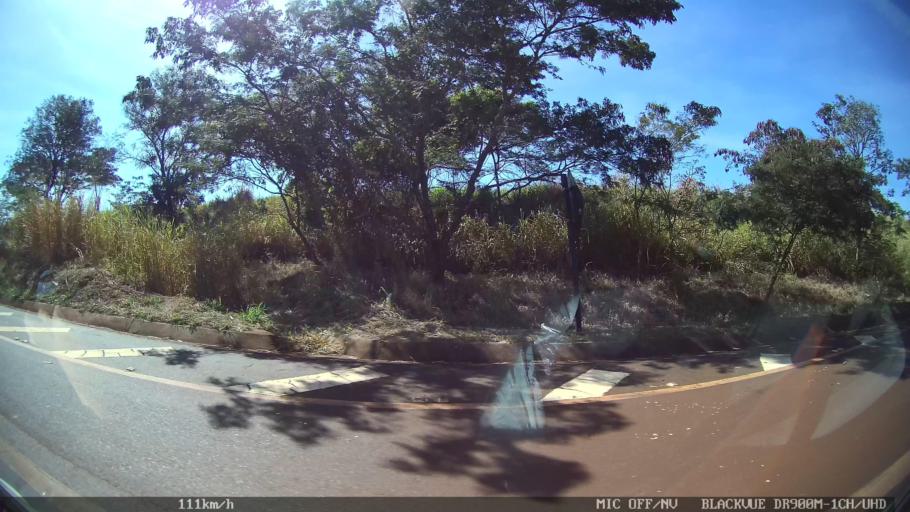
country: BR
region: Sao Paulo
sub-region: Sao Joaquim Da Barra
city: Sao Joaquim da Barra
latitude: -20.5355
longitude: -47.8268
